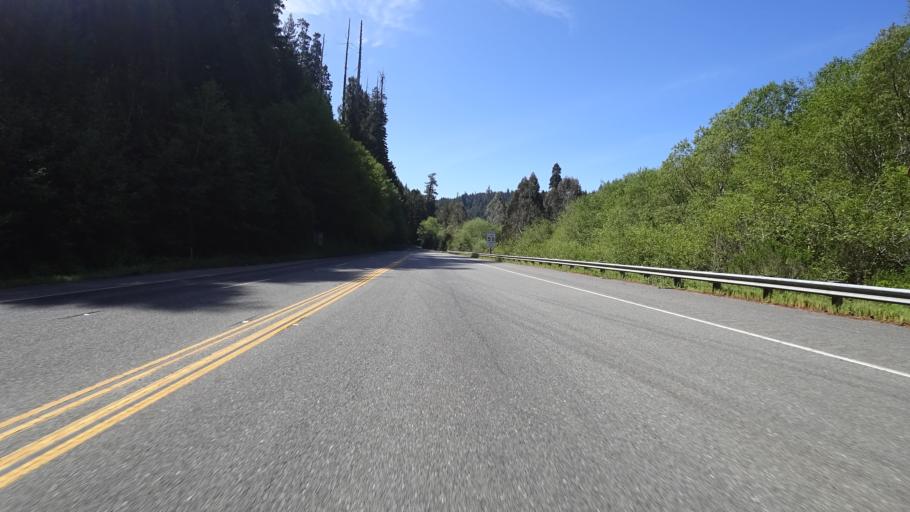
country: US
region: California
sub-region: Humboldt County
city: Westhaven-Moonstone
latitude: 41.3459
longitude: -124.0297
